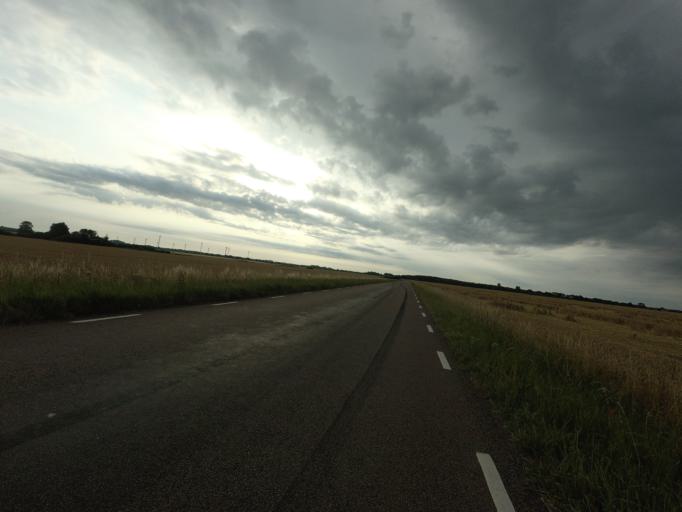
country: SE
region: Skane
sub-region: Helsingborg
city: Odakra
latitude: 56.1558
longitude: 12.7134
